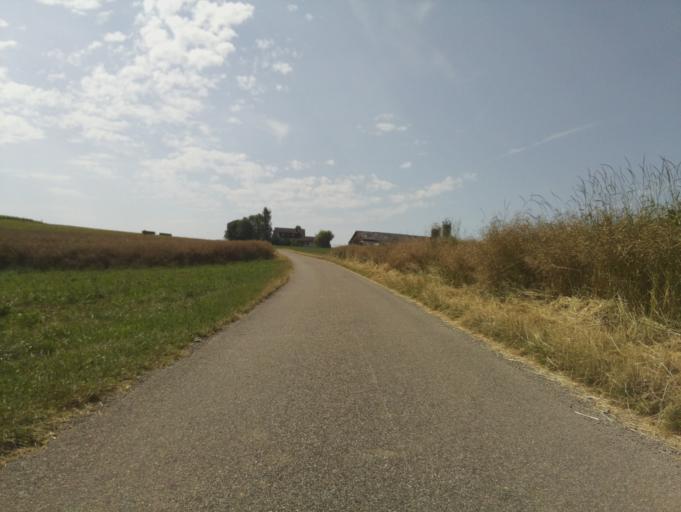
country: CH
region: Zurich
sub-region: Bezirk Andelfingen
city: Grossandelfingen
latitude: 47.5855
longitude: 8.6683
